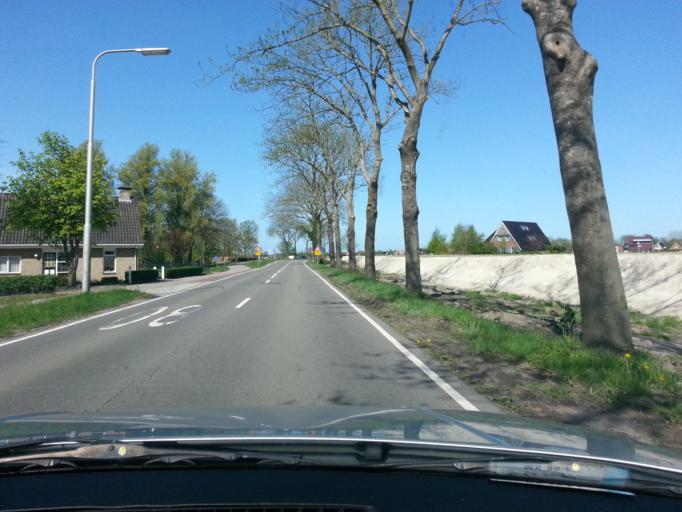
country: NL
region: Friesland
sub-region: Gemeente Achtkarspelen
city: Buitenpost
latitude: 53.2407
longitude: 6.1637
